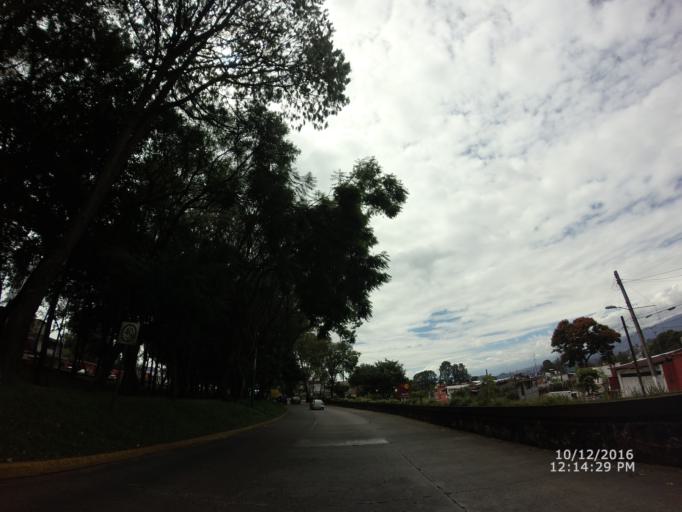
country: MX
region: Veracruz
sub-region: Xalapa
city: Xalapa de Enriquez
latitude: 19.5498
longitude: -96.9300
